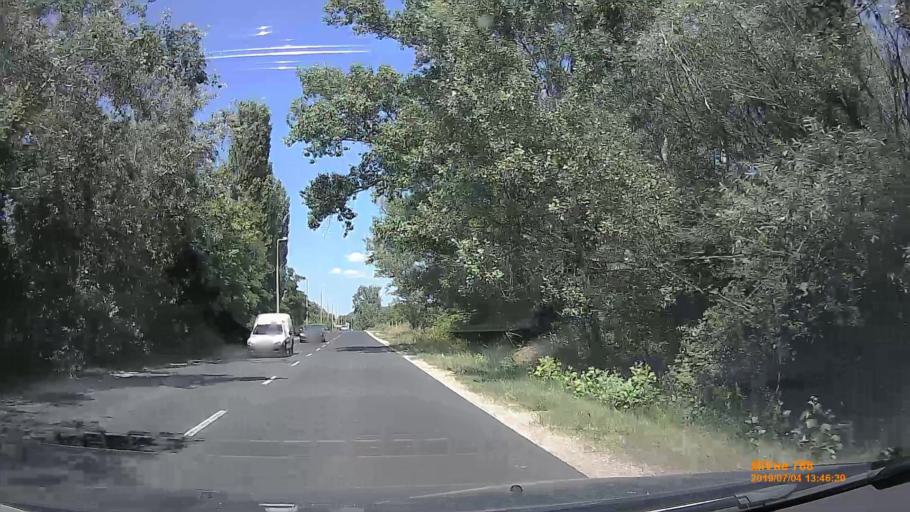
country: HU
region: Komarom-Esztergom
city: Tatabanya
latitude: 47.5873
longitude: 18.3788
